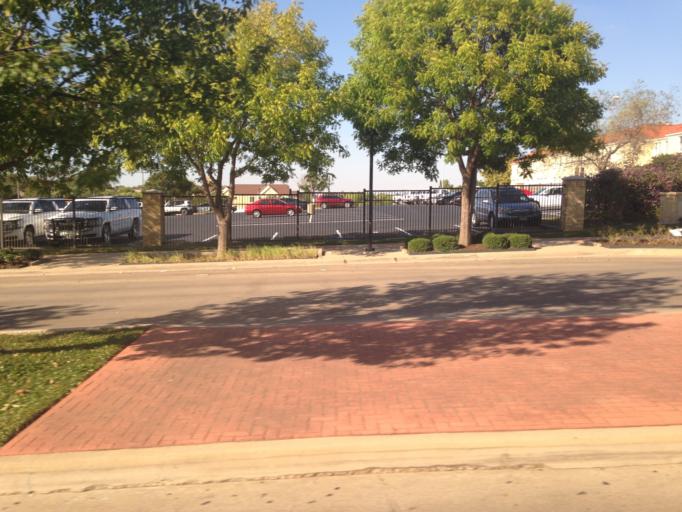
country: US
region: Texas
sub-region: Tarrant County
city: Fort Worth
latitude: 32.7061
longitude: -97.3539
